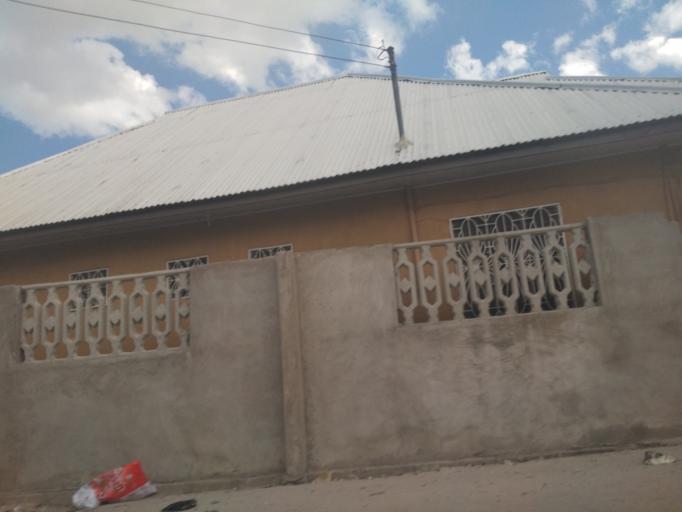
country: TZ
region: Dar es Salaam
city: Dar es Salaam
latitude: -6.8718
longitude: 39.2338
